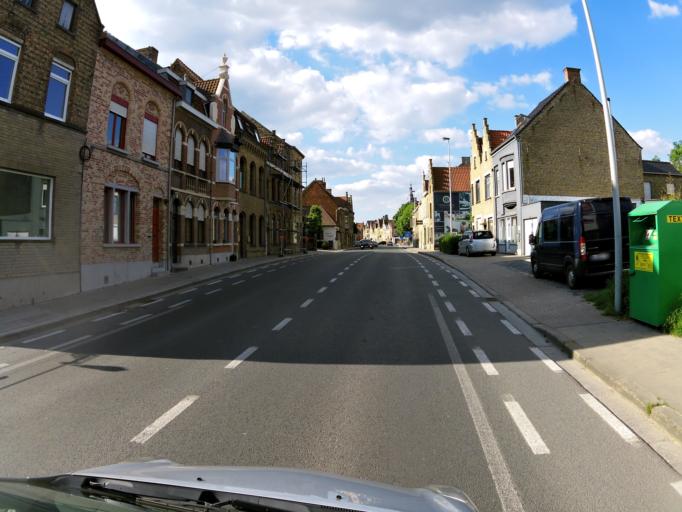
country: BE
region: Flanders
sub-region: Provincie West-Vlaanderen
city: Diksmuide
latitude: 51.0299
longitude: 2.8640
